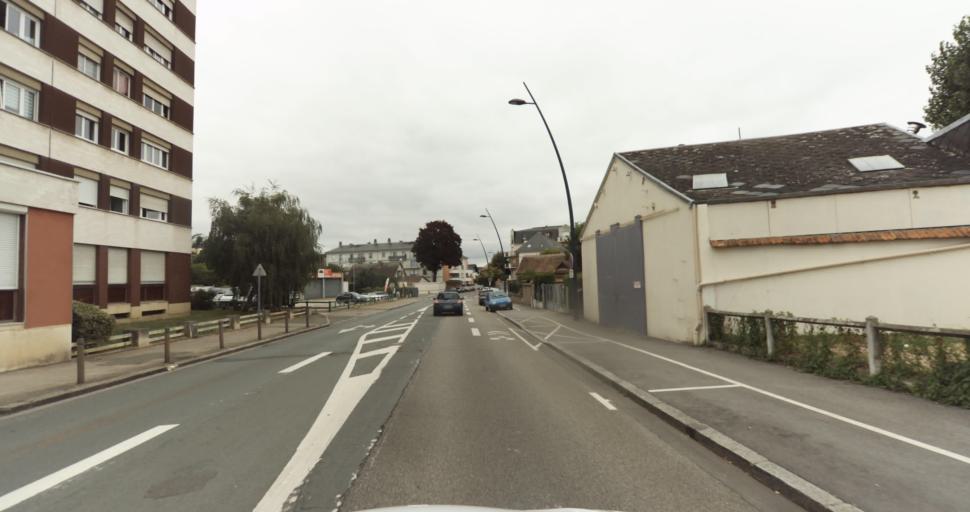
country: FR
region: Haute-Normandie
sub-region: Departement de l'Eure
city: Evreux
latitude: 49.0277
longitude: 1.1555
